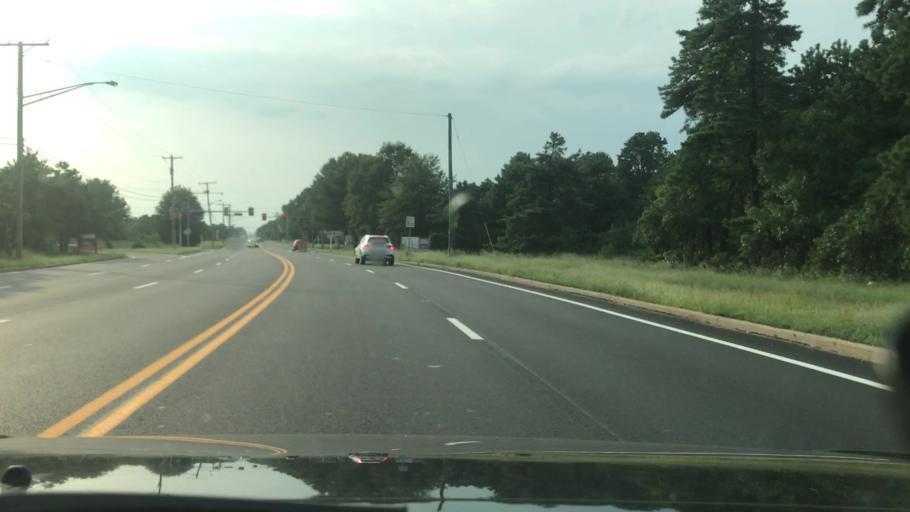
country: US
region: New Jersey
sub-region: Ocean County
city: Leisure Village
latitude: 40.0682
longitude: -74.1656
